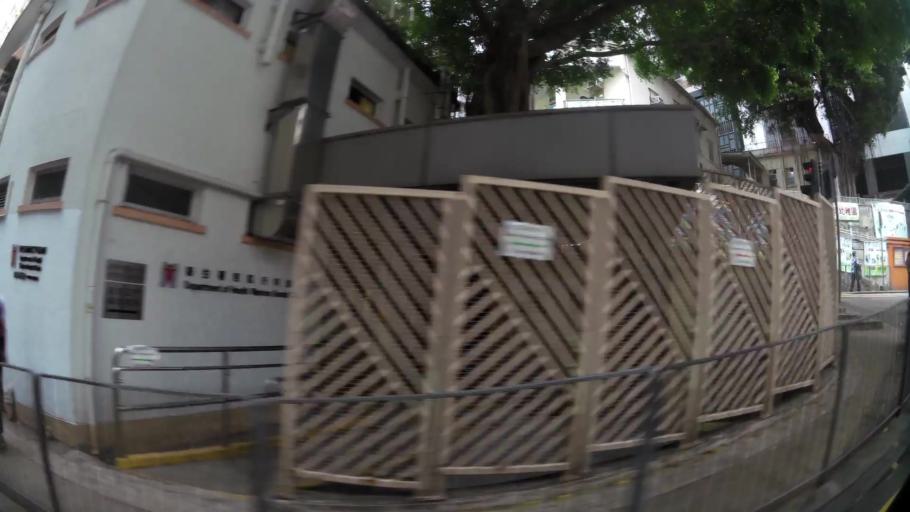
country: HK
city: Hong Kong
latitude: 22.2853
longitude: 114.1392
